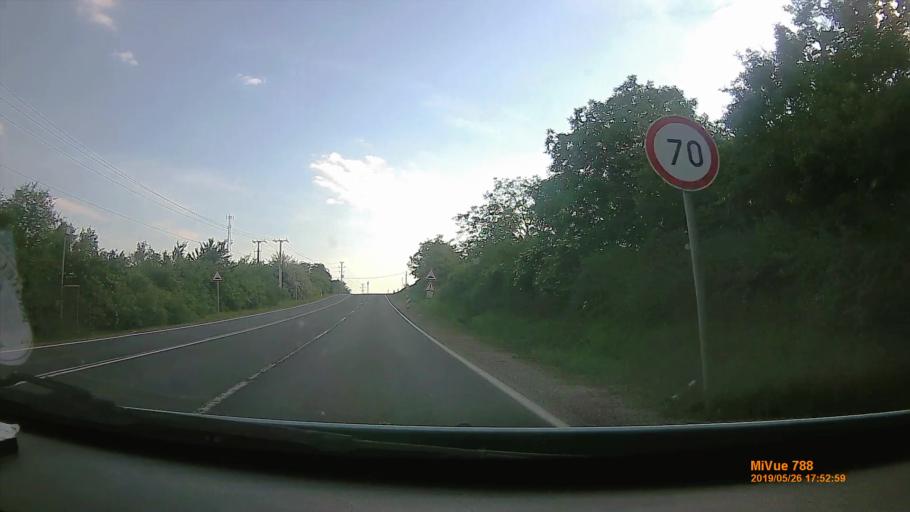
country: HU
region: Borsod-Abauj-Zemplen
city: Onga
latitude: 48.1579
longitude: 20.9014
